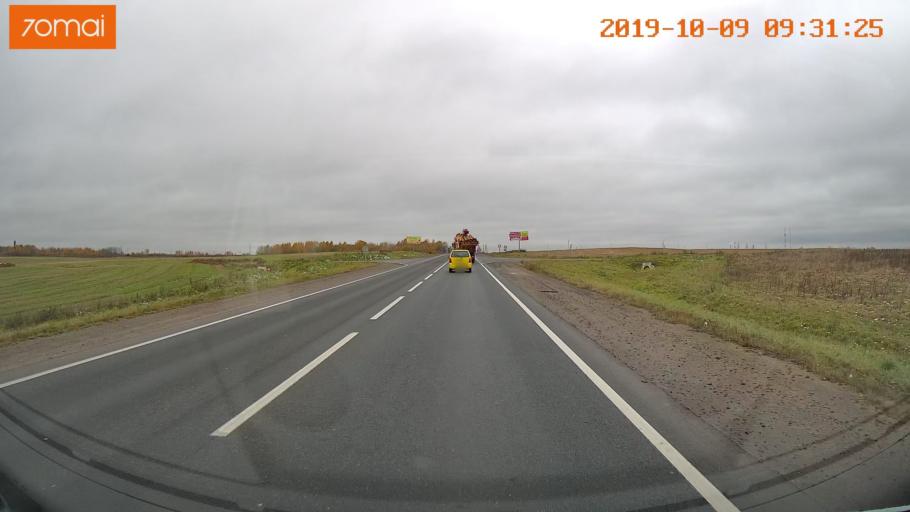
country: RU
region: Vologda
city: Vologda
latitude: 59.1494
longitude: 39.9388
